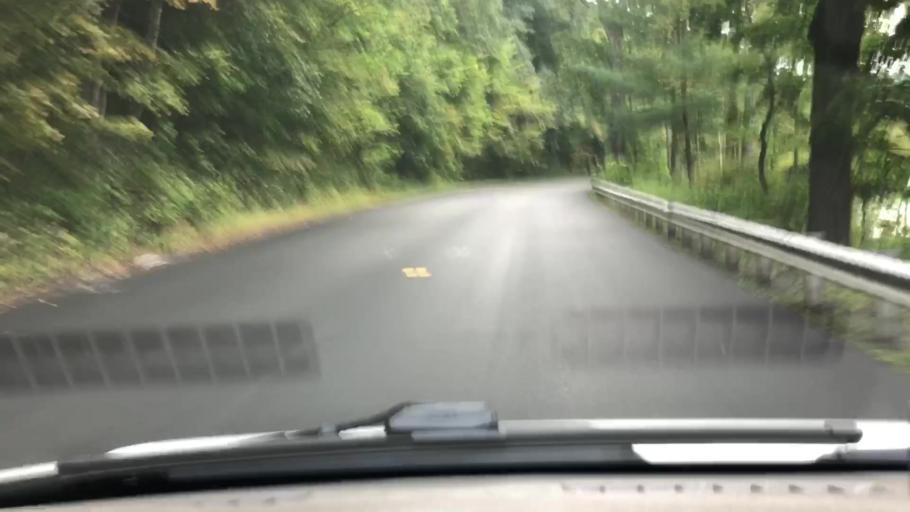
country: US
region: Massachusetts
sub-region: Franklin County
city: Charlemont
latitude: 42.6256
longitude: -72.8526
